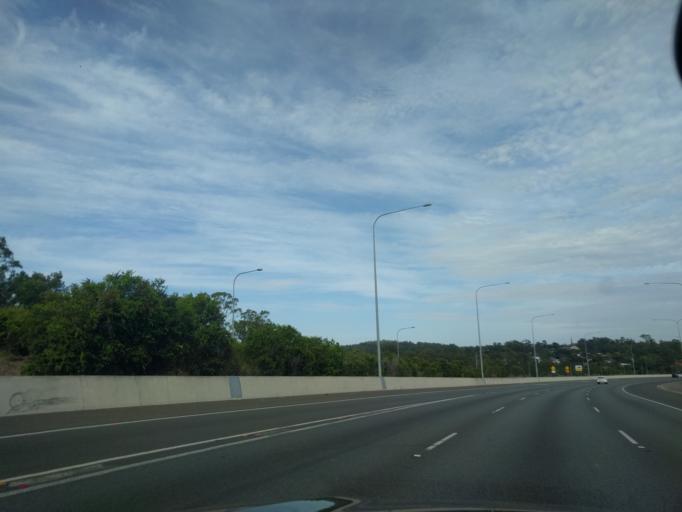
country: AU
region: Queensland
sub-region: Ipswich
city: Redbank
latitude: -27.6041
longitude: 152.8627
